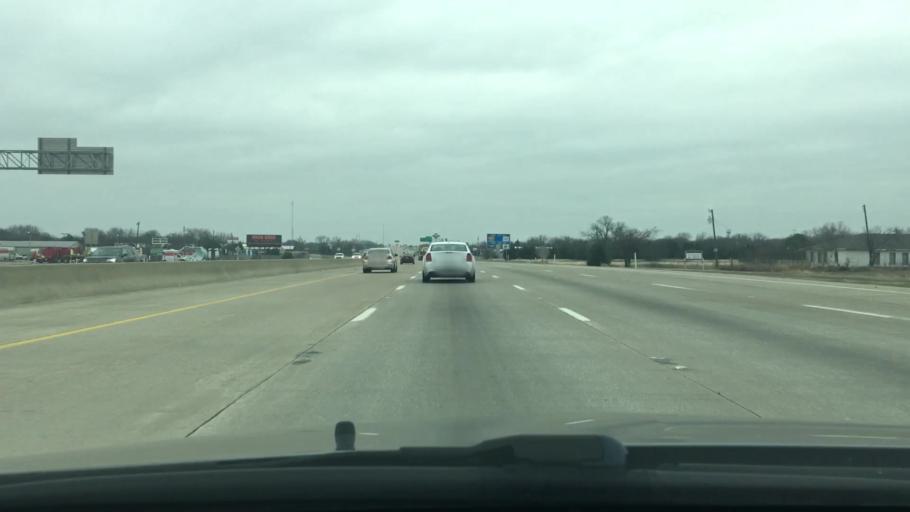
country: US
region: Texas
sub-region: Dallas County
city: Wilmer
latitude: 32.6043
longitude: -96.6862
